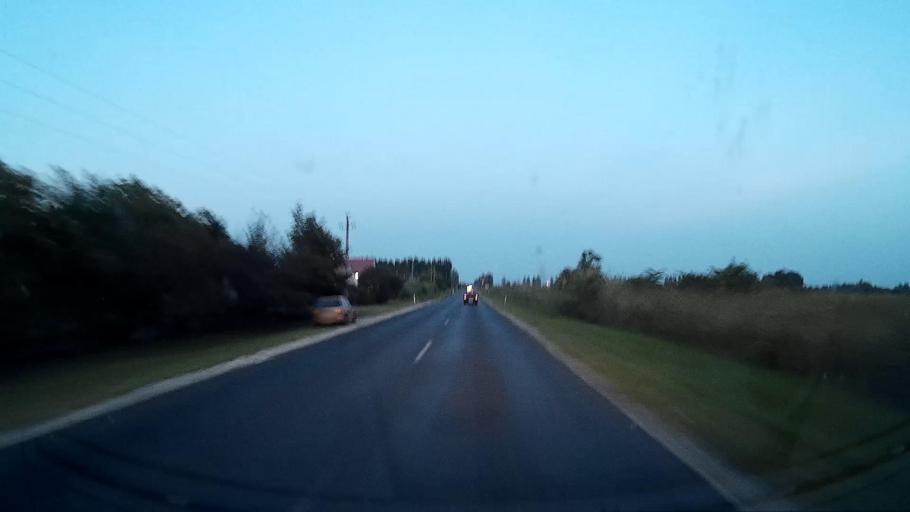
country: HU
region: Pest
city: Cegled
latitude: 47.1832
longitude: 19.7557
